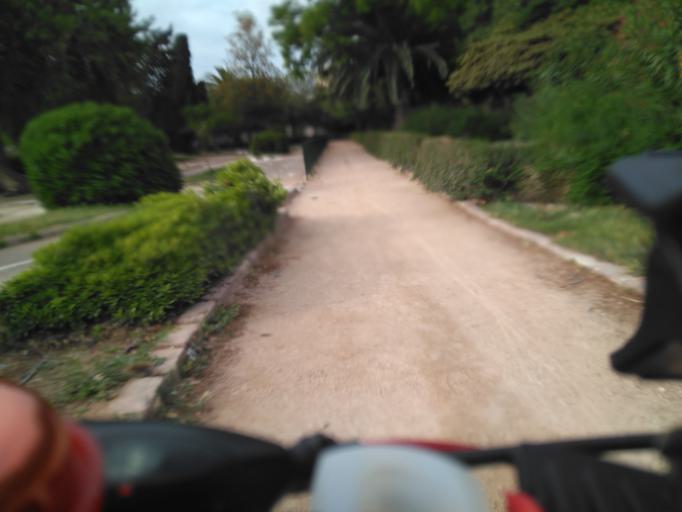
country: ES
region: Valencia
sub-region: Provincia de Valencia
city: Valencia
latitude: 39.4804
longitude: -0.3678
